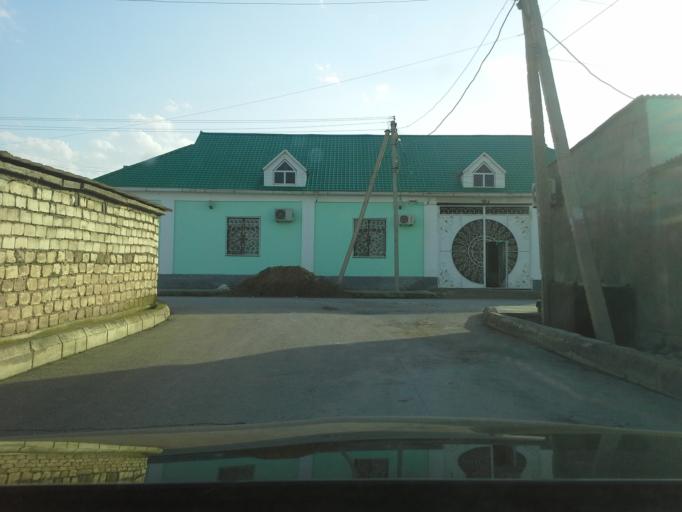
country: TM
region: Ahal
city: Abadan
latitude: 38.0293
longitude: 58.2262
